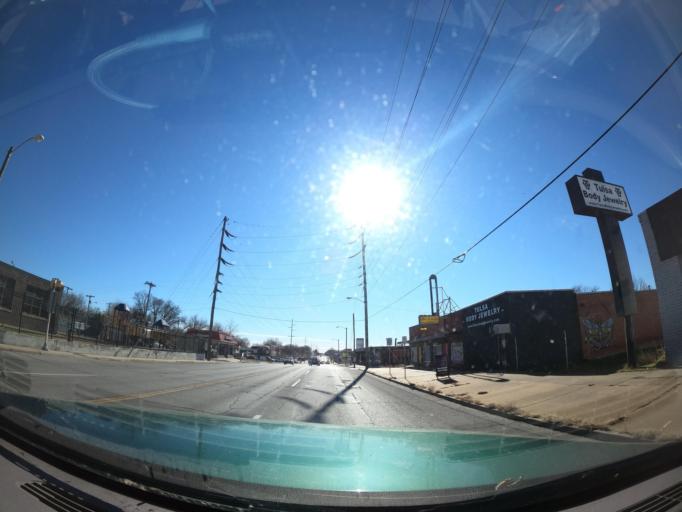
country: US
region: Oklahoma
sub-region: Tulsa County
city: Tulsa
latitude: 36.1355
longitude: -95.9404
